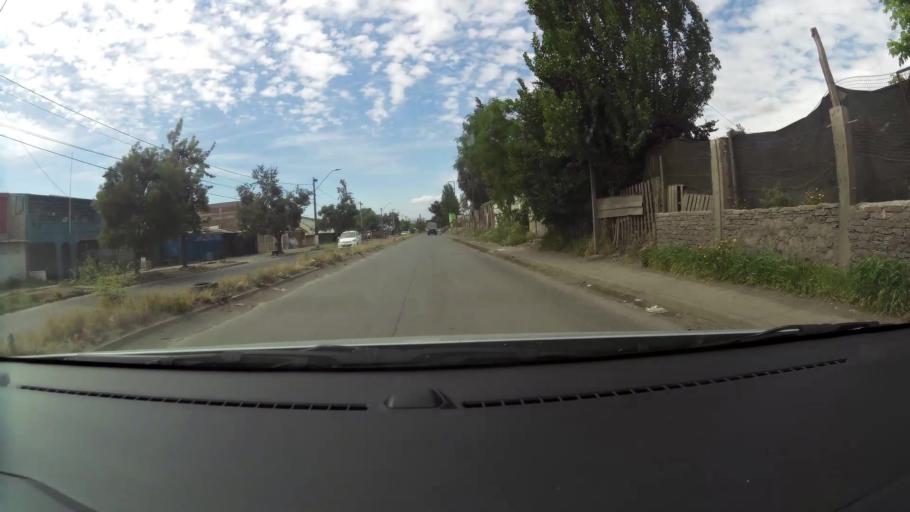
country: CL
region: Santiago Metropolitan
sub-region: Provincia de Santiago
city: La Pintana
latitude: -33.5891
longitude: -70.6644
